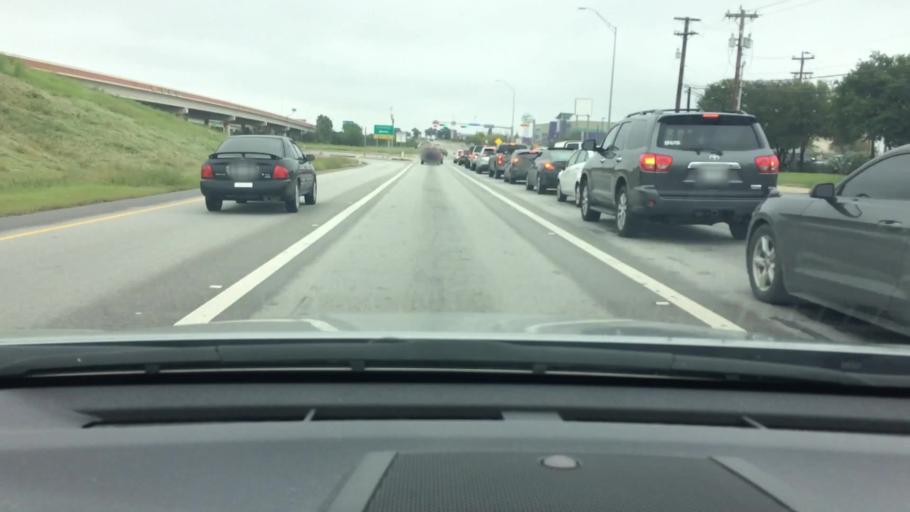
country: US
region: Texas
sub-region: Bexar County
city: Leon Valley
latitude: 29.4928
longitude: -98.7047
